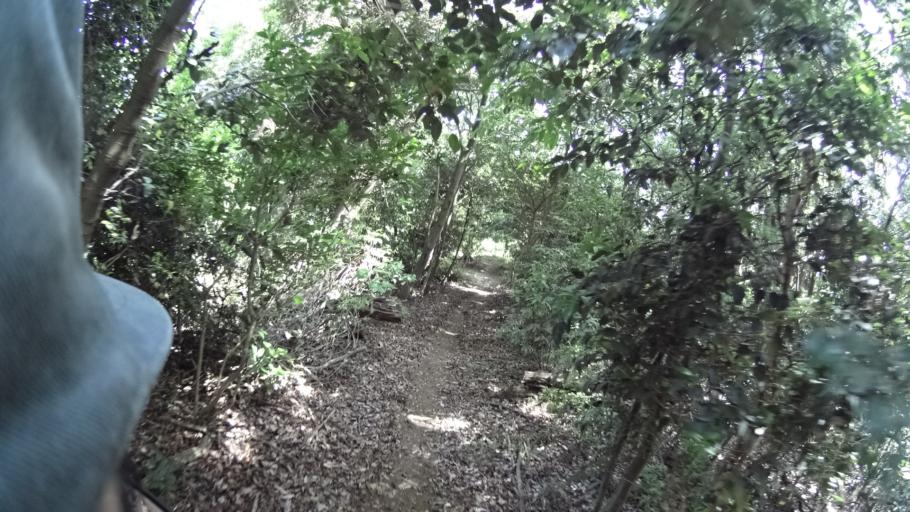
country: JP
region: Shizuoka
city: Kosai-shi
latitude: 34.7834
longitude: 137.4963
